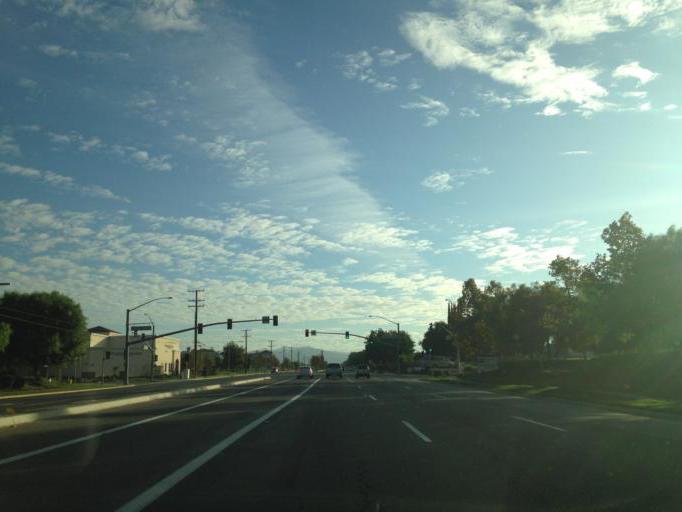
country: US
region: California
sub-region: Riverside County
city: Temecula
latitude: 33.4773
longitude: -117.1129
